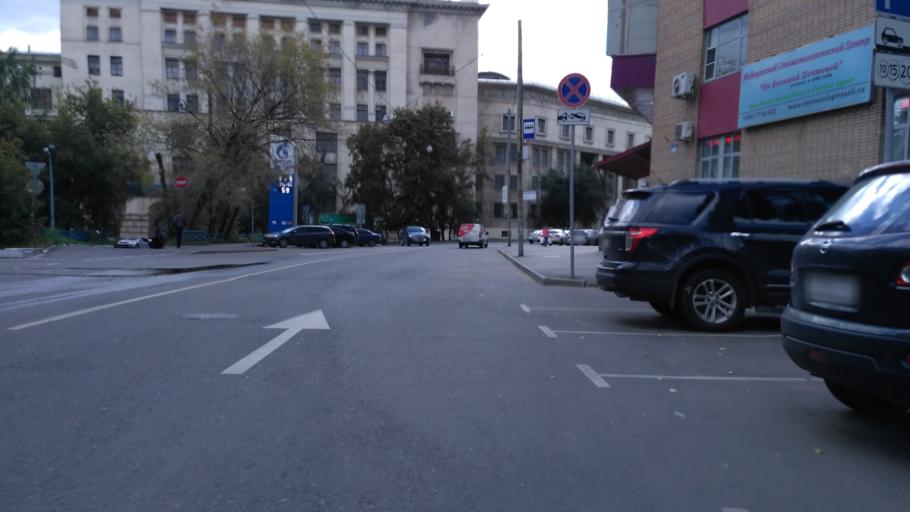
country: RU
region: Moscow
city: Lefortovo
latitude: 55.7792
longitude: 37.6969
